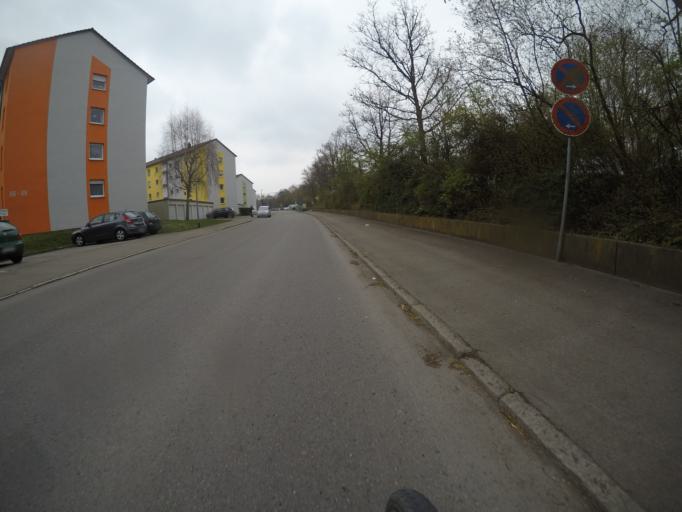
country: DE
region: Baden-Wuerttemberg
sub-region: Regierungsbezirk Stuttgart
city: Boeblingen
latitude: 48.6810
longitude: 8.9981
